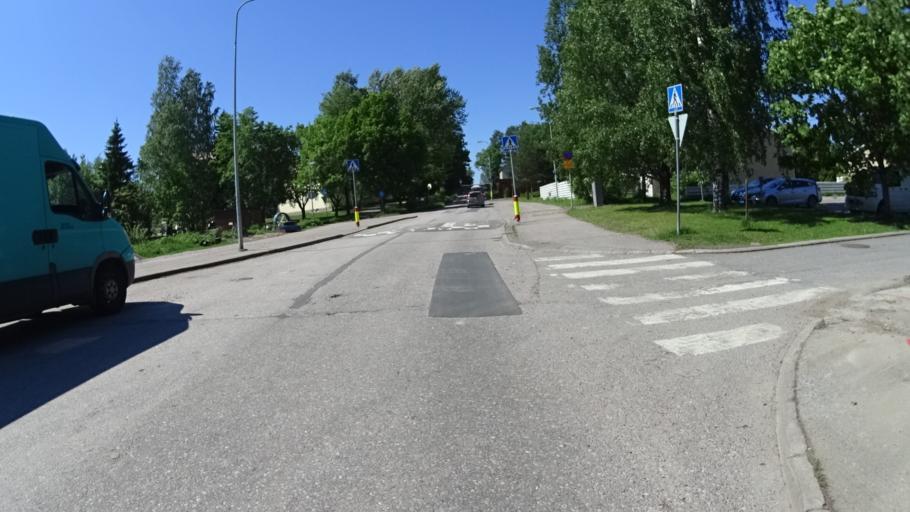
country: FI
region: Uusimaa
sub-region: Helsinki
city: Kilo
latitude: 60.2662
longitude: 24.7878
